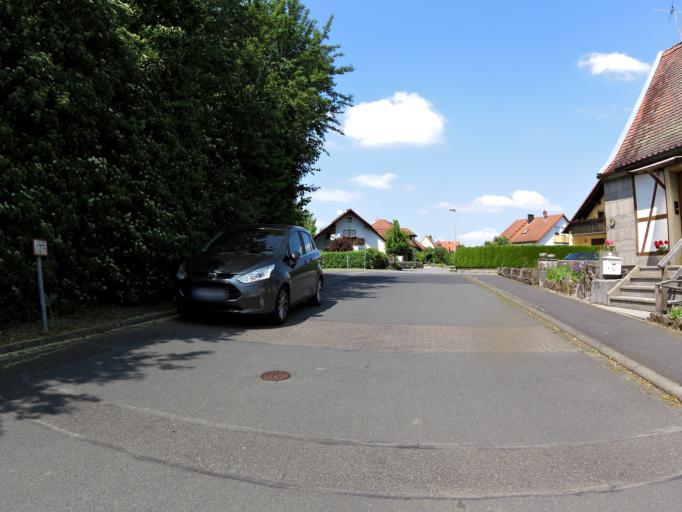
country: DE
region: Bavaria
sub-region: Regierungsbezirk Unterfranken
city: Kleinrinderfeld
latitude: 49.7015
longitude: 9.8391
